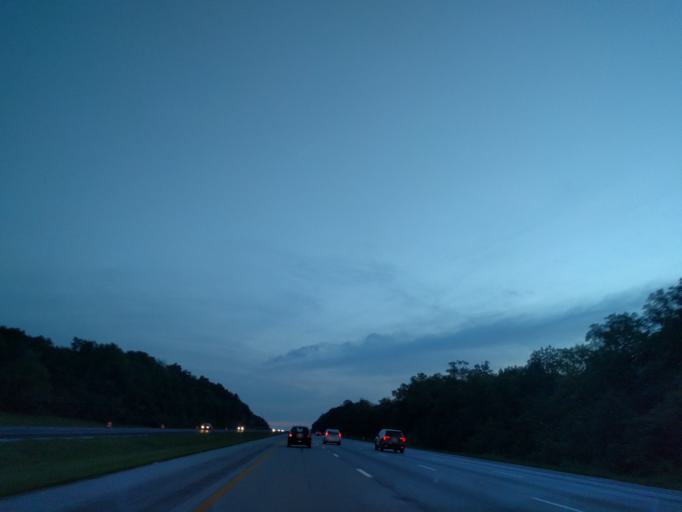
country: US
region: Kentucky
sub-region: Hardin County
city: Elizabethtown
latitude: 37.7363
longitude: -85.8060
